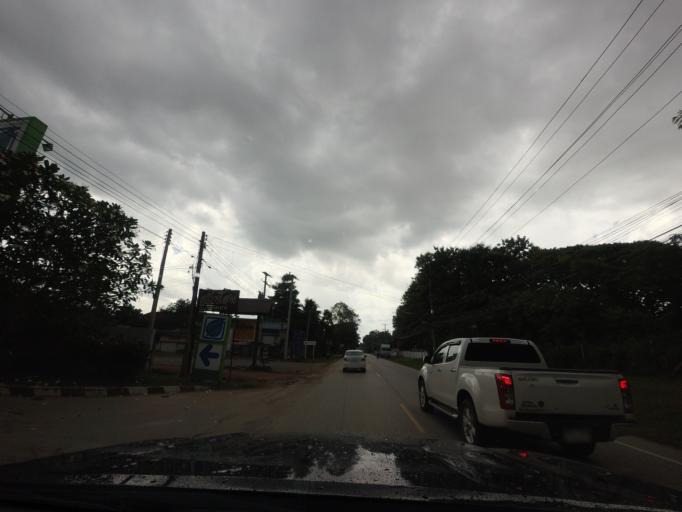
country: LA
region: Vientiane
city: Muang Sanakham
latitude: 17.8974
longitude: 101.6734
